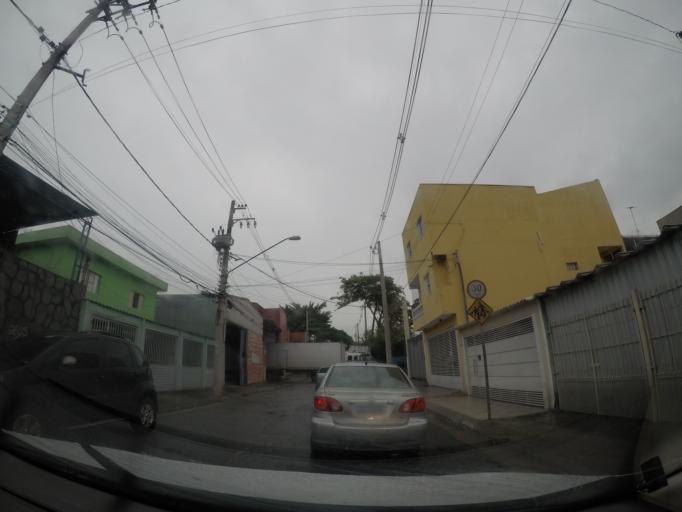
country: BR
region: Sao Paulo
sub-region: Guarulhos
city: Guarulhos
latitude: -23.4515
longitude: -46.4790
